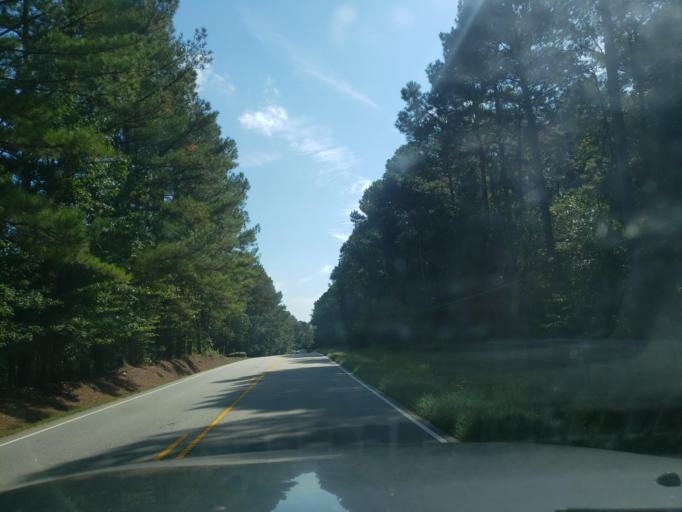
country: US
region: North Carolina
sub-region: Durham County
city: Gorman
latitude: 35.9329
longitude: -78.7112
